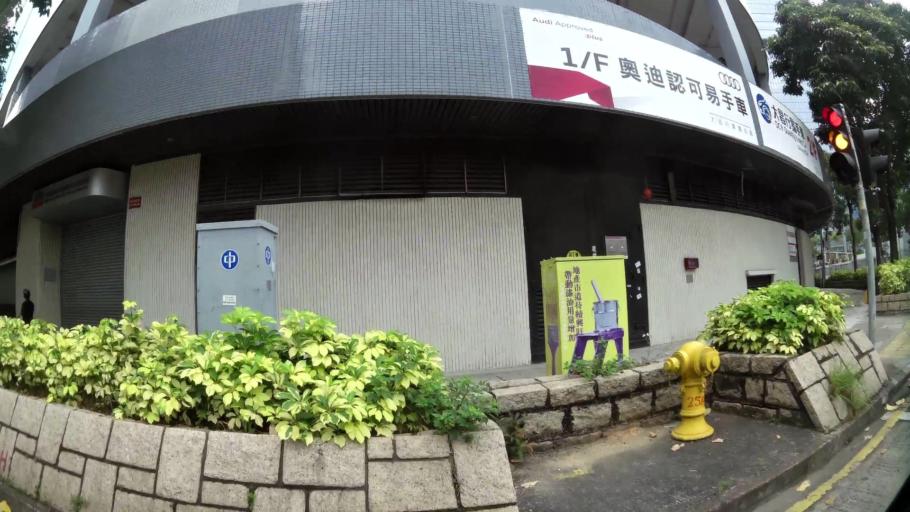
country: HK
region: Kowloon City
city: Kowloon
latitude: 22.3254
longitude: 114.2088
